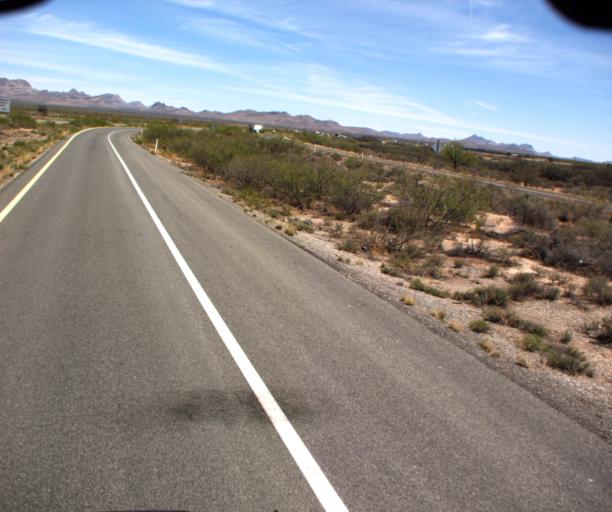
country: US
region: New Mexico
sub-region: Hidalgo County
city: Lordsburg
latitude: 32.2564
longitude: -109.1913
